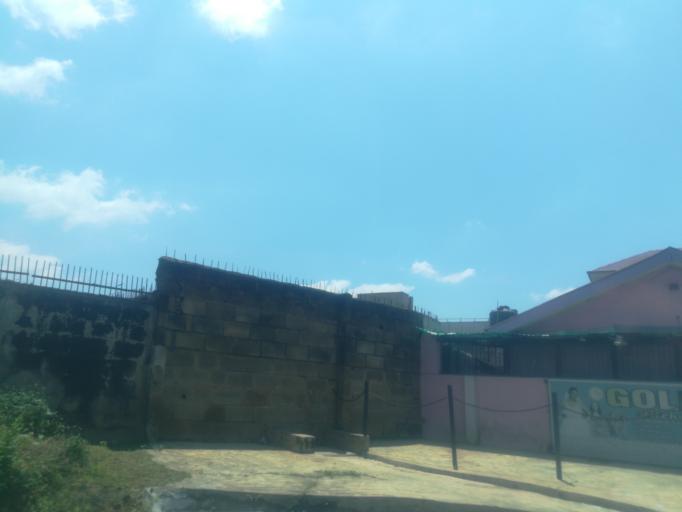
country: NG
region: Oyo
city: Ibadan
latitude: 7.3612
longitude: 3.8707
